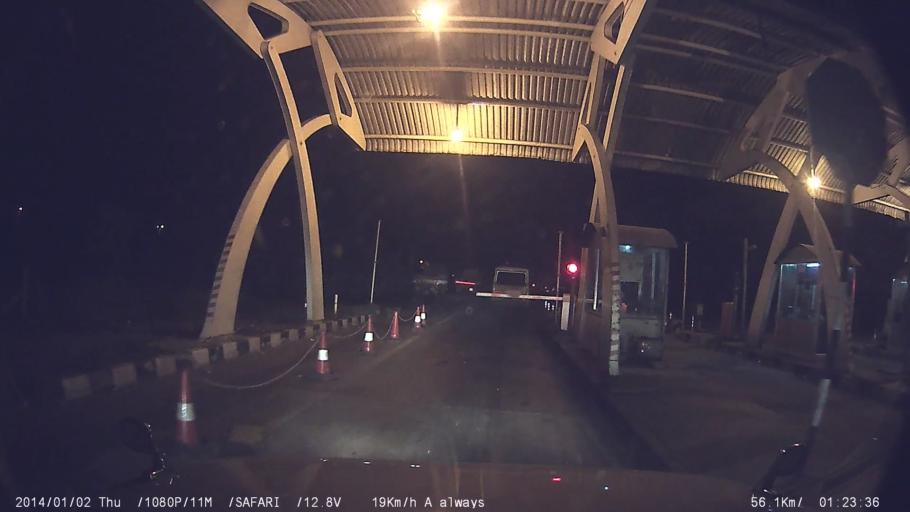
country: IN
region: Tamil Nadu
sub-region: Coimbatore
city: Irugur
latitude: 11.0608
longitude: 77.0888
